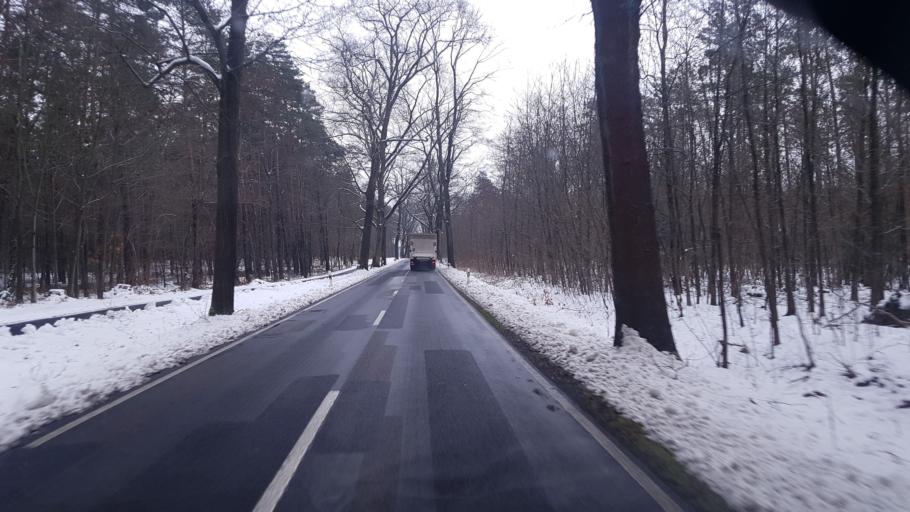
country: DE
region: Brandenburg
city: Lawitz
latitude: 52.0814
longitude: 14.5255
